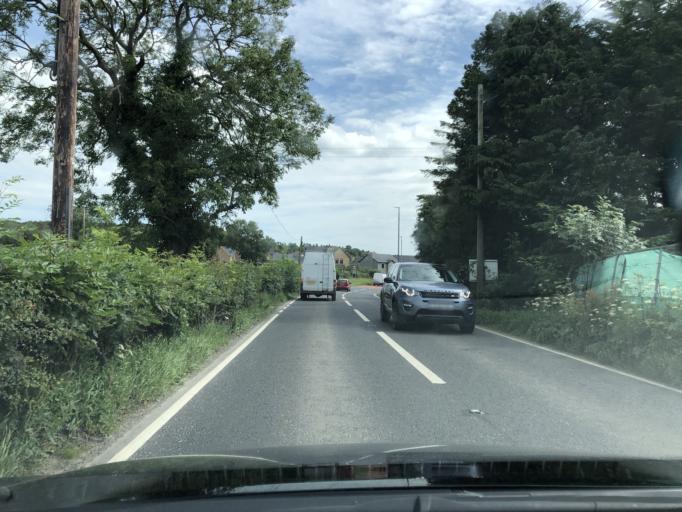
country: GB
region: Northern Ireland
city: Ballynahinch
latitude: 54.4136
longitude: -5.9045
